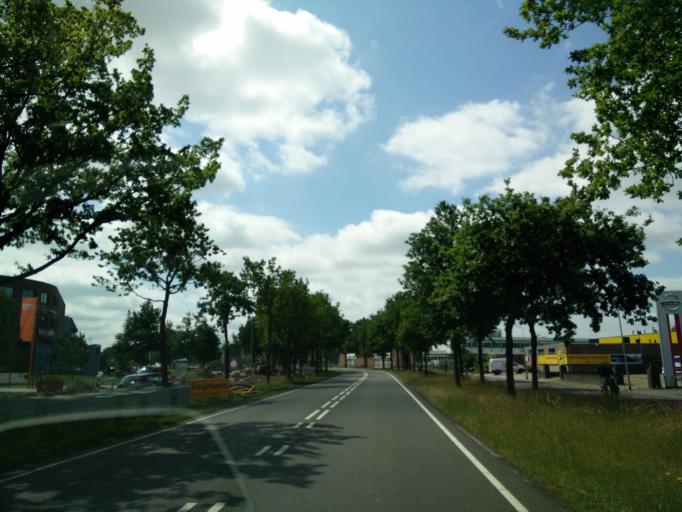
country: NL
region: Drenthe
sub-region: Gemeente Assen
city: Assen
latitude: 53.0057
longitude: 6.5695
